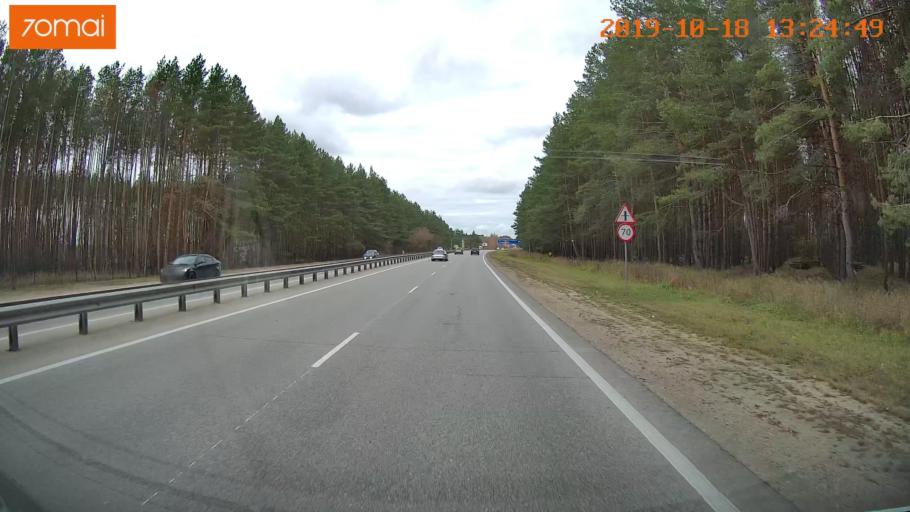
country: RU
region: Rjazan
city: Polyany
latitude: 54.7362
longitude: 39.8419
